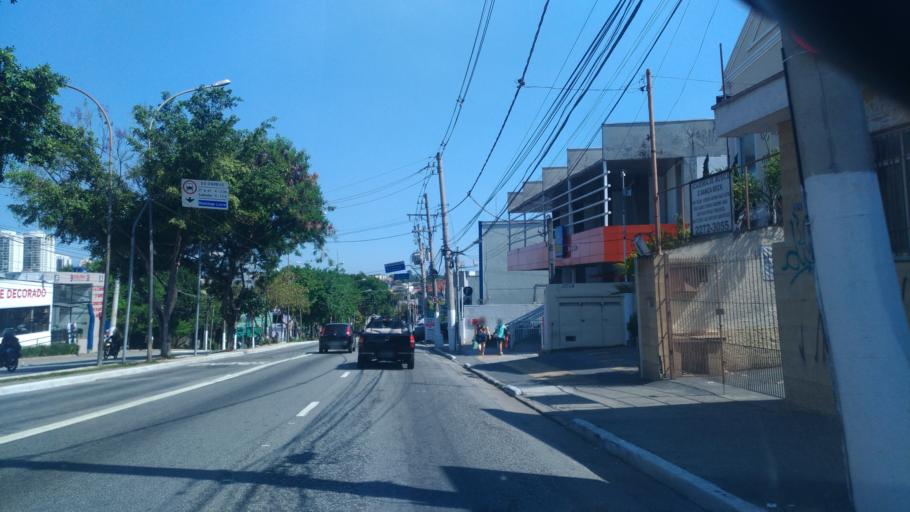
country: BR
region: Sao Paulo
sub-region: Sao Caetano Do Sul
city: Sao Caetano do Sul
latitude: -23.5803
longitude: -46.5869
